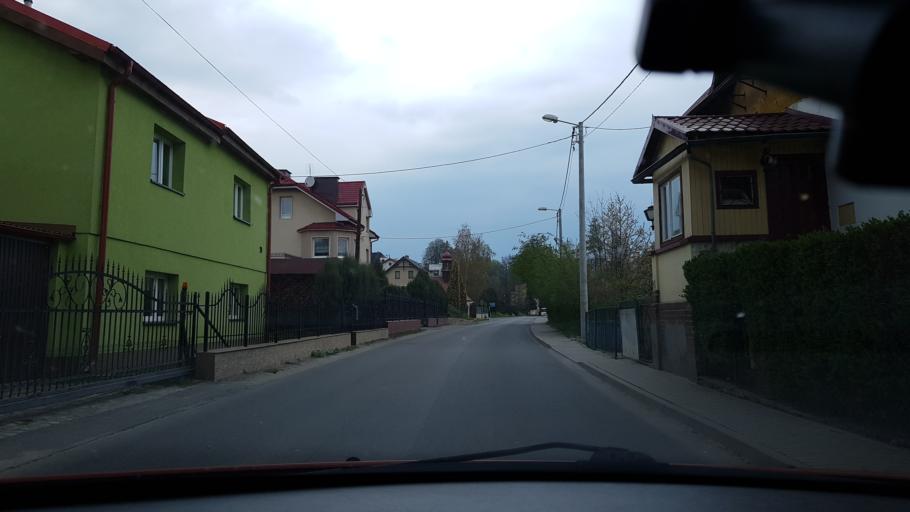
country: PL
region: Lower Silesian Voivodeship
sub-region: Powiat klodzki
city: Klodzko
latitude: 50.4214
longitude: 16.6417
